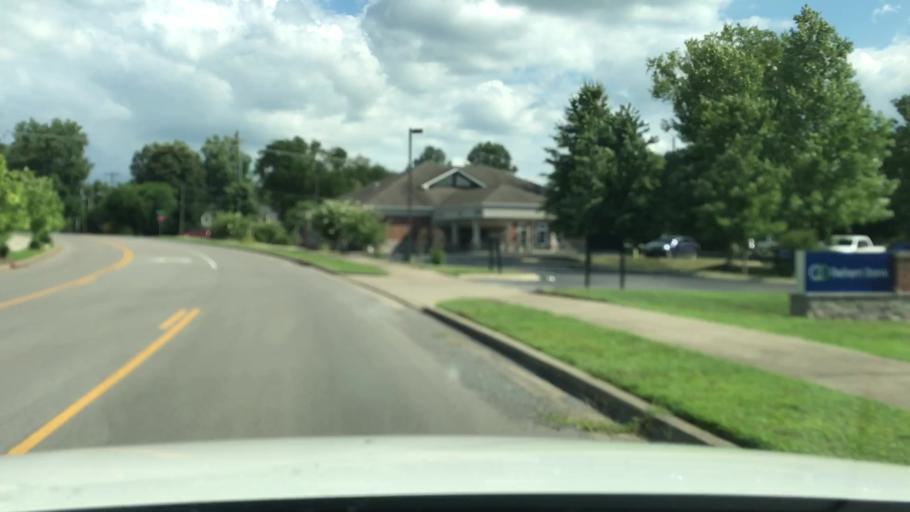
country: US
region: Tennessee
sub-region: Sumner County
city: Gallatin
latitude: 36.3720
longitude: -86.4836
